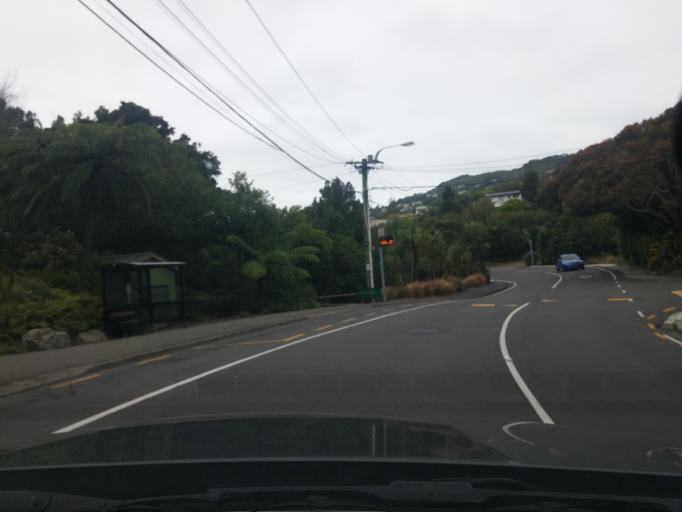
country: NZ
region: Wellington
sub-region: Wellington City
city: Kelburn
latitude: -41.2683
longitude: 174.7567
